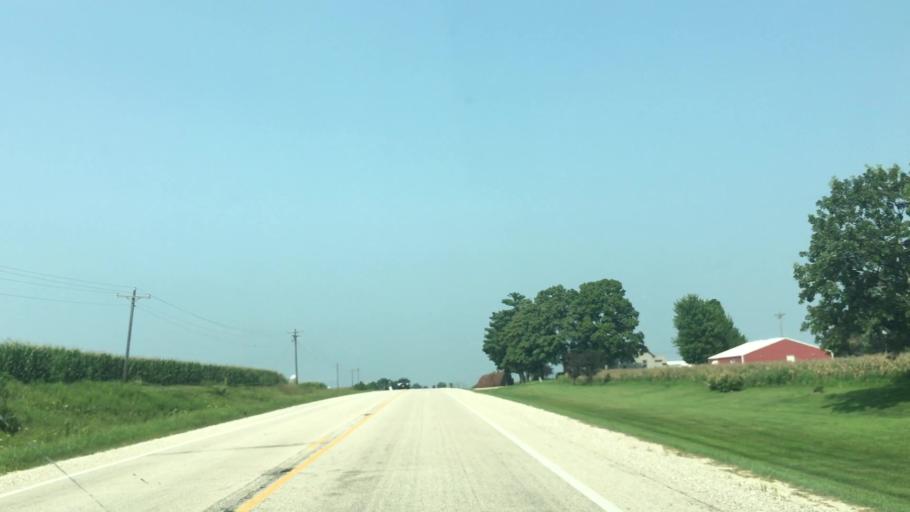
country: US
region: Iowa
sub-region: Fayette County
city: West Union
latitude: 43.0070
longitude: -91.8243
